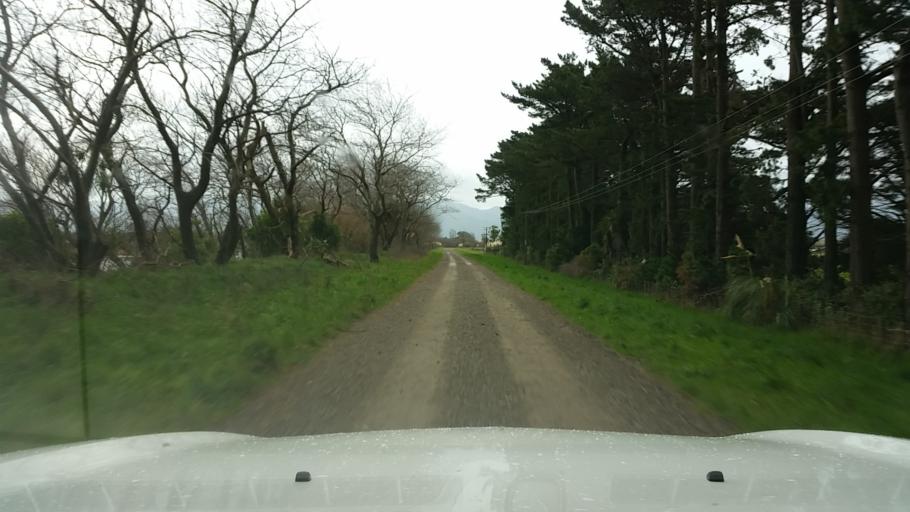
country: NZ
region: Wellington
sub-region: Upper Hutt City
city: Upper Hutt
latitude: -41.2922
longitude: 175.2204
